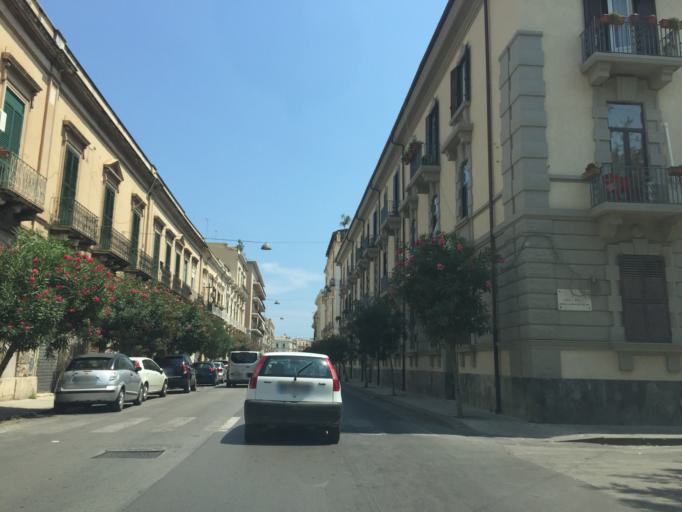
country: IT
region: Sicily
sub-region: Provincia di Siracusa
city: Siracusa
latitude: 37.0653
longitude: 15.2869
